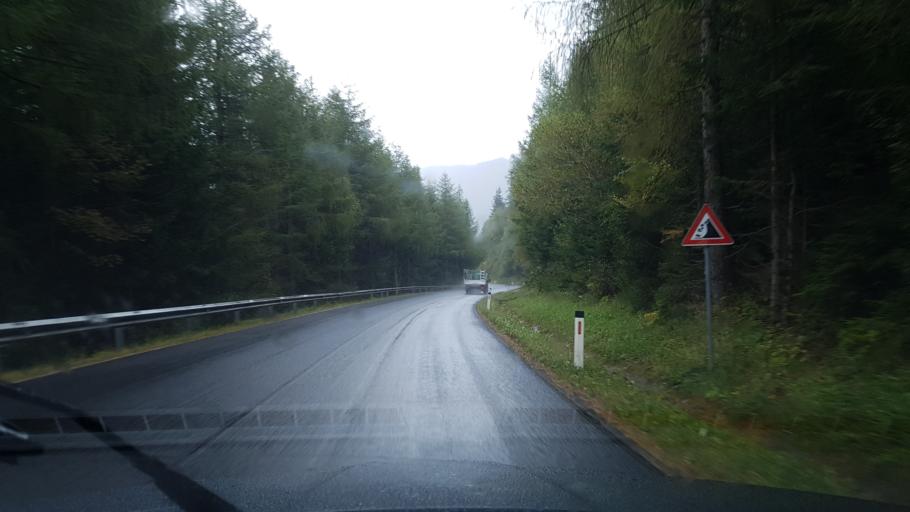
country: AT
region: Styria
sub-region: Politischer Bezirk Voitsberg
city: Salla
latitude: 47.1079
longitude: 14.9541
